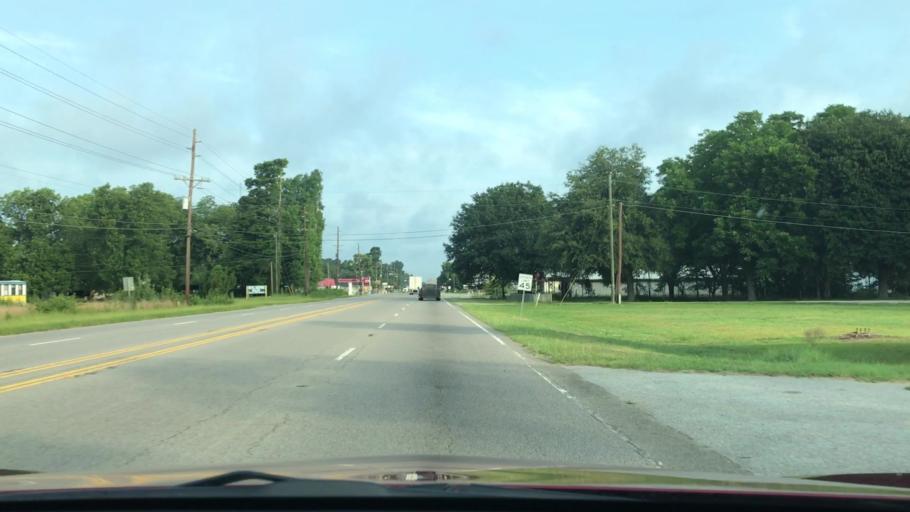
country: US
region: South Carolina
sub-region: Orangeburg County
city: Brookdale
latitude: 33.4755
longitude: -80.8133
